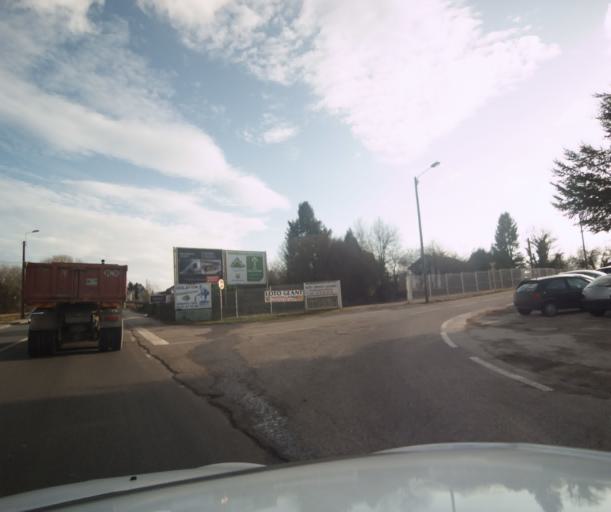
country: FR
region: Franche-Comte
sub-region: Departement du Doubs
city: Besancon
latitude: 47.2614
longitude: 6.0071
